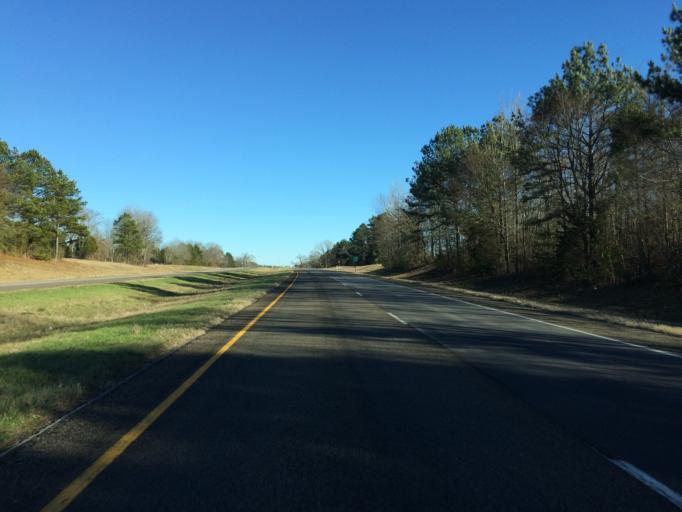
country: US
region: Texas
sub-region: Wood County
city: Hawkins
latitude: 32.5968
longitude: -95.2519
